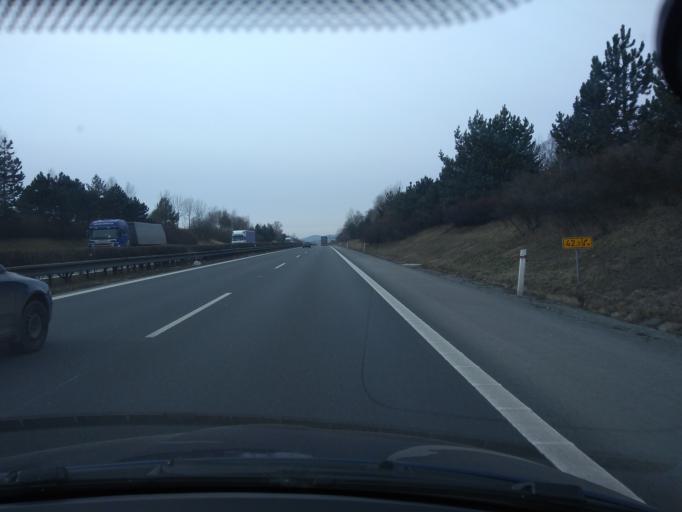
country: CZ
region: Plzensky
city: Zbiroh
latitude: 49.8388
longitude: 13.8022
